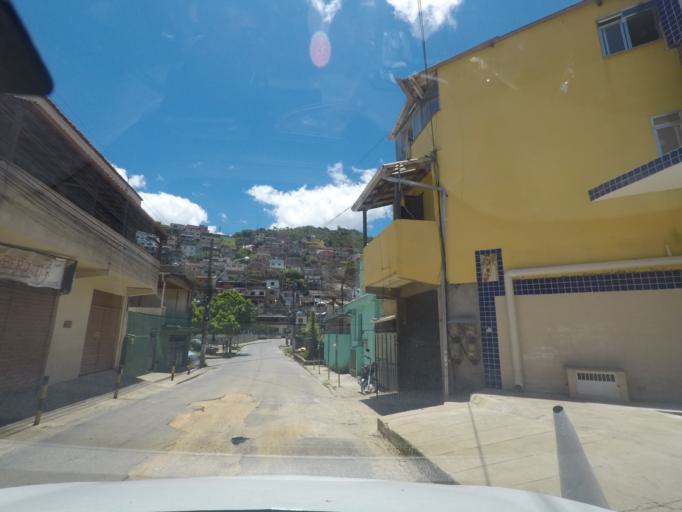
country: BR
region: Rio de Janeiro
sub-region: Teresopolis
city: Teresopolis
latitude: -22.4305
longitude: -42.9676
